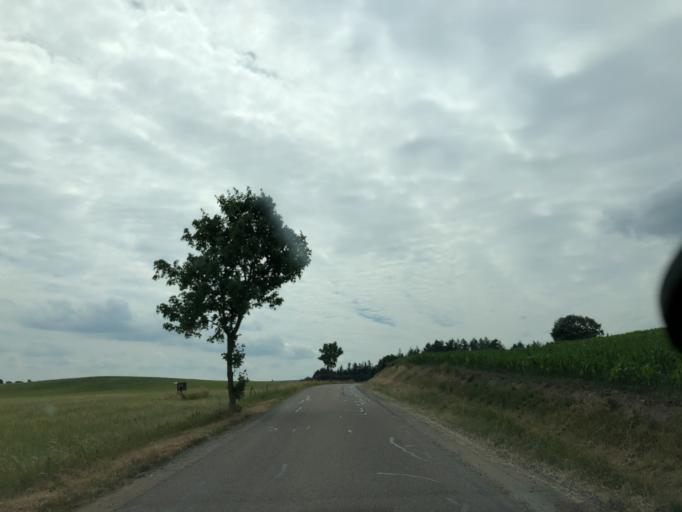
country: DK
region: Central Jutland
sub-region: Silkeborg Kommune
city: Svejbaek
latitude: 56.1993
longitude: 9.6902
